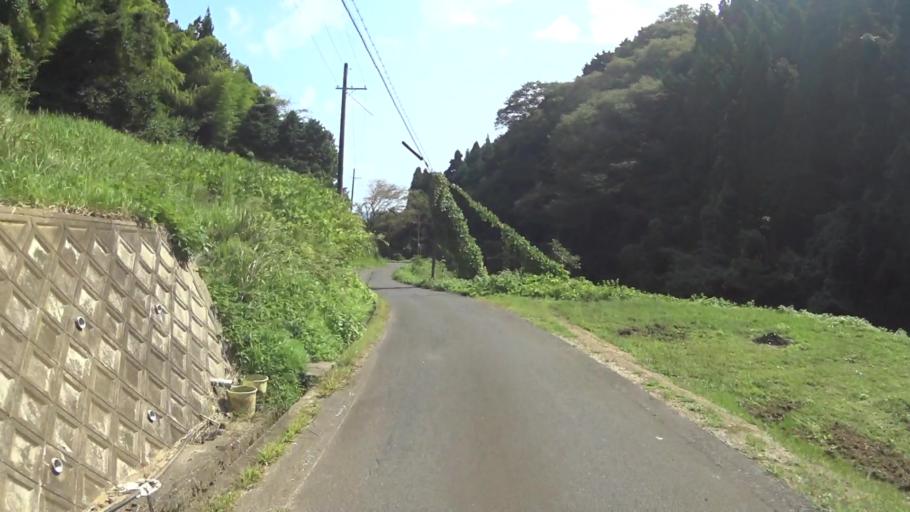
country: JP
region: Kyoto
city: Miyazu
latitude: 35.6556
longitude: 135.2545
